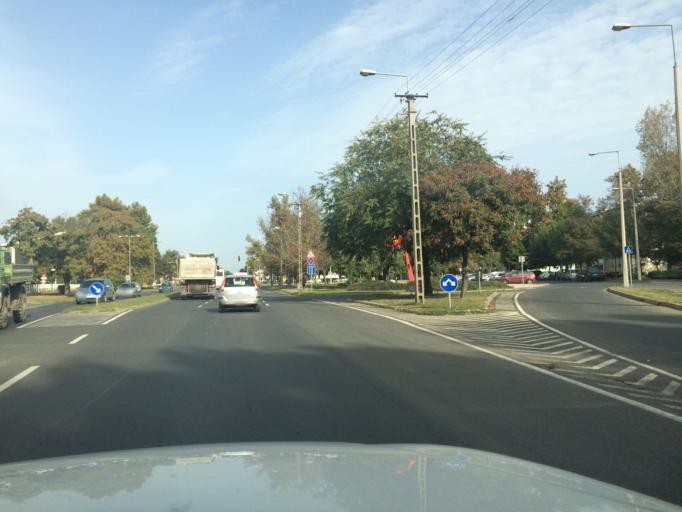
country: HU
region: Szabolcs-Szatmar-Bereg
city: Nyiregyhaza
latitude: 47.9453
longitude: 21.7073
